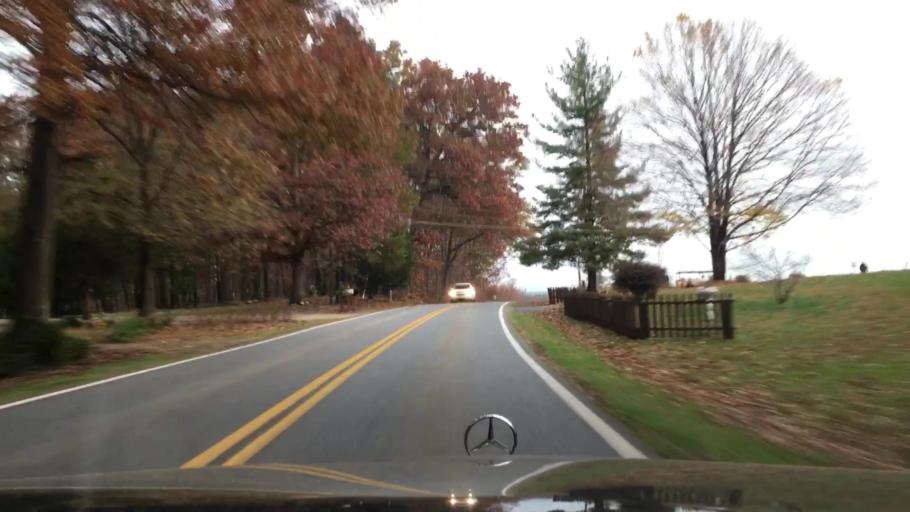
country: US
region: Virginia
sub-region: Campbell County
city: Altavista
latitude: 37.1538
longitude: -79.2978
